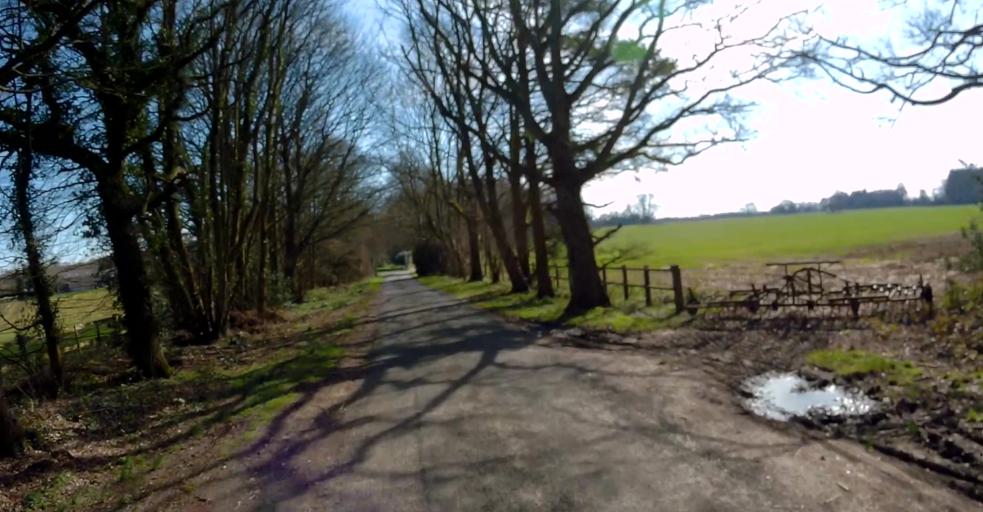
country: GB
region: England
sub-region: Hampshire
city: Four Marks
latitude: 51.1833
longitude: -1.0710
